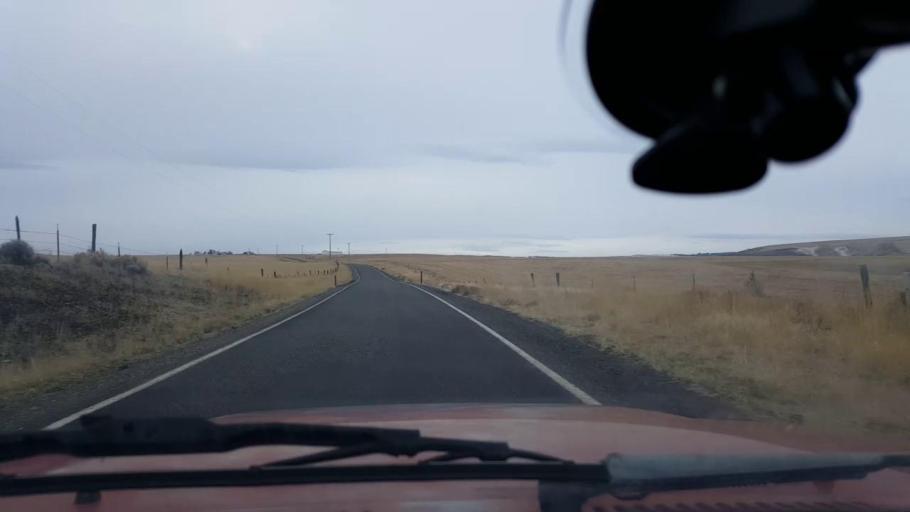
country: US
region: Washington
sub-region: Asotin County
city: Clarkston Heights-Vineland
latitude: 46.3291
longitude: -117.3223
